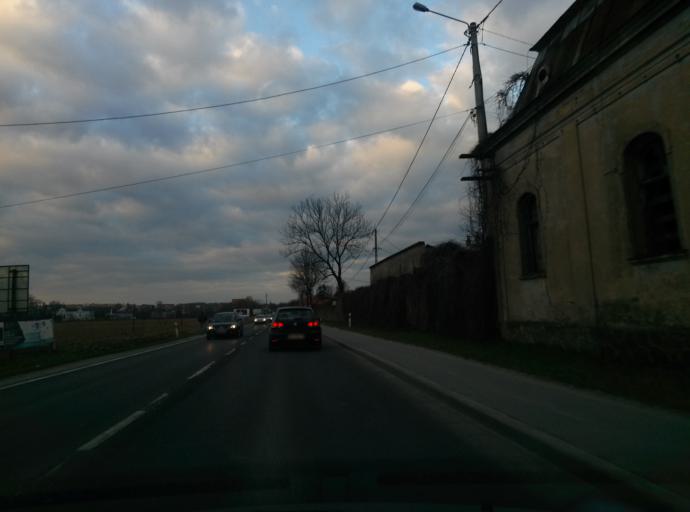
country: PL
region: Lesser Poland Voivodeship
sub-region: Powiat brzeski
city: Okocim
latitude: 49.9582
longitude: 20.5939
